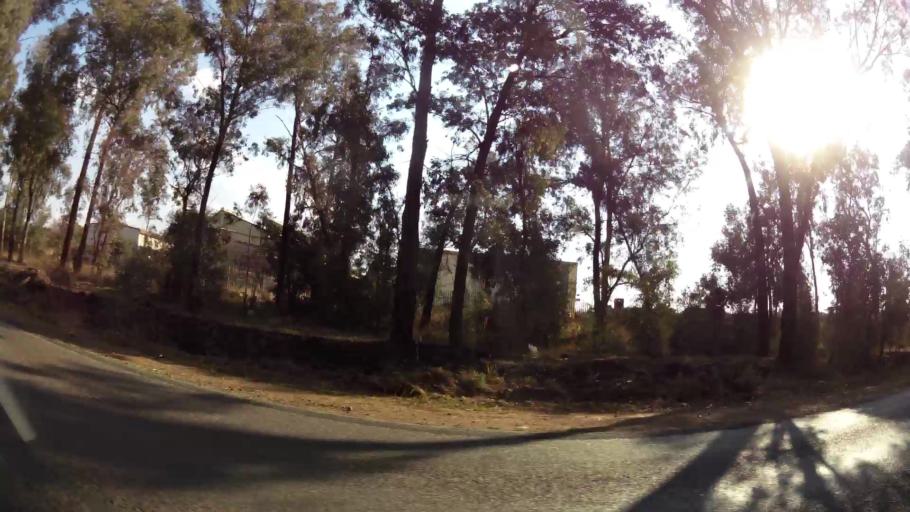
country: ZA
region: Gauteng
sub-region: Ekurhuleni Metropolitan Municipality
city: Tembisa
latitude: -25.9380
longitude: 28.2328
